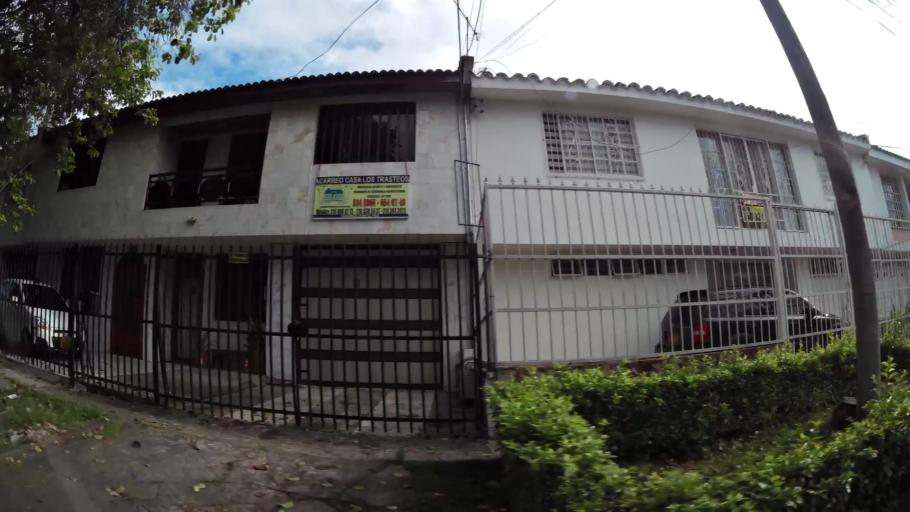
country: CO
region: Valle del Cauca
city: Cali
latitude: 3.4857
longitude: -76.5207
